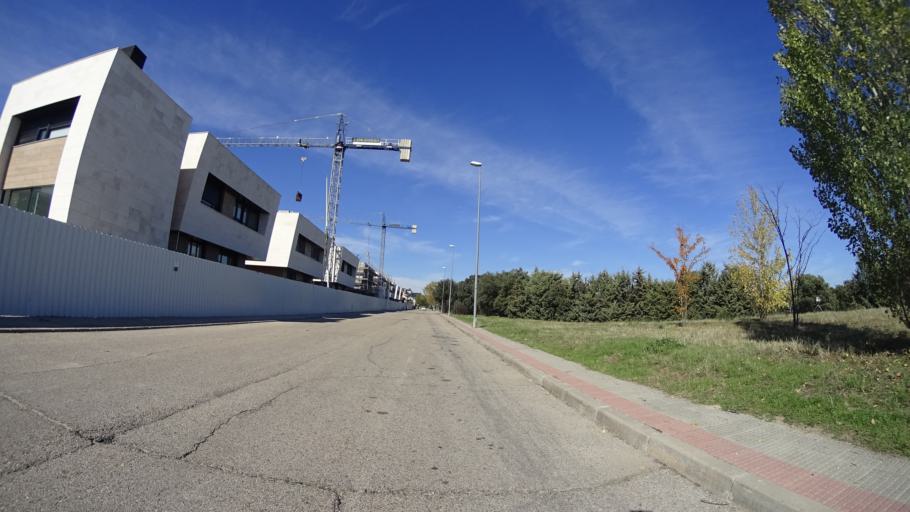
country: ES
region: Madrid
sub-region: Provincia de Madrid
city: Villanueva del Pardillo
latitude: 40.4928
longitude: -3.9582
